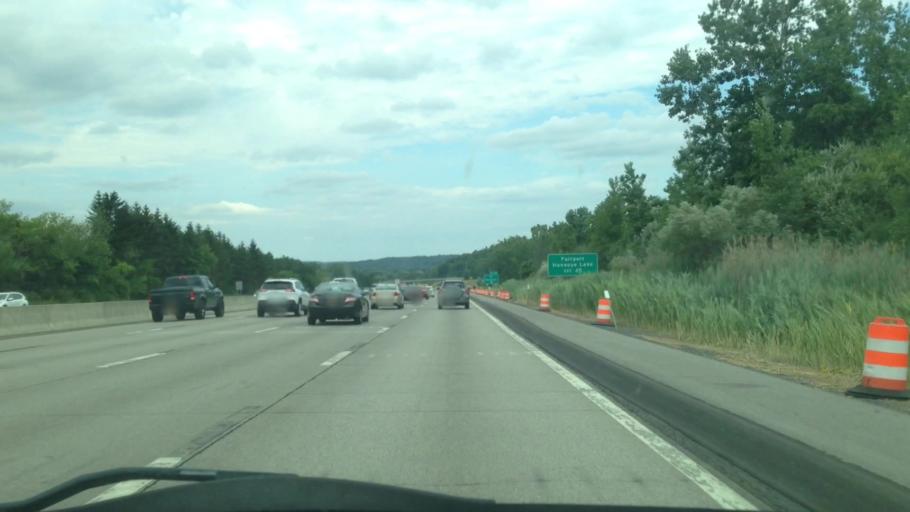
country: US
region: New York
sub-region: Ontario County
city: Victor
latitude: 43.0038
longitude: -77.4308
